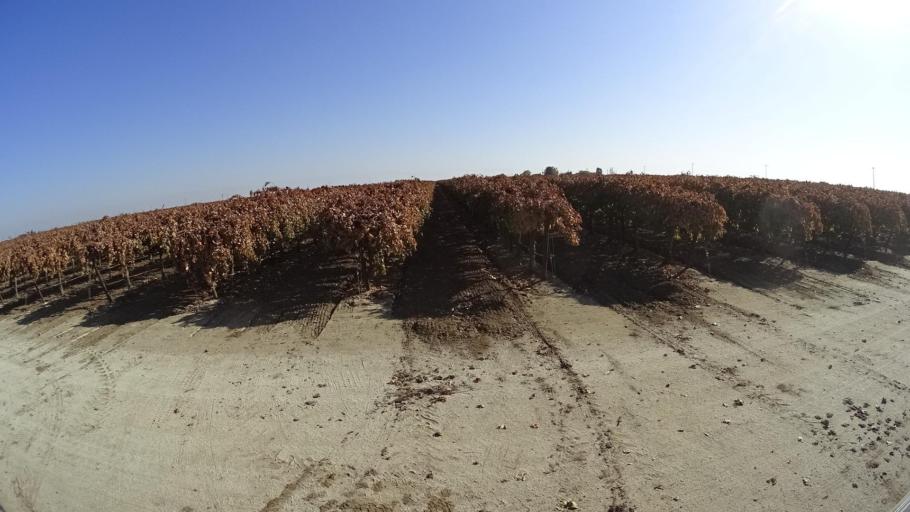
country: US
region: California
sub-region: Kern County
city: Delano
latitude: 35.7410
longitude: -119.2142
